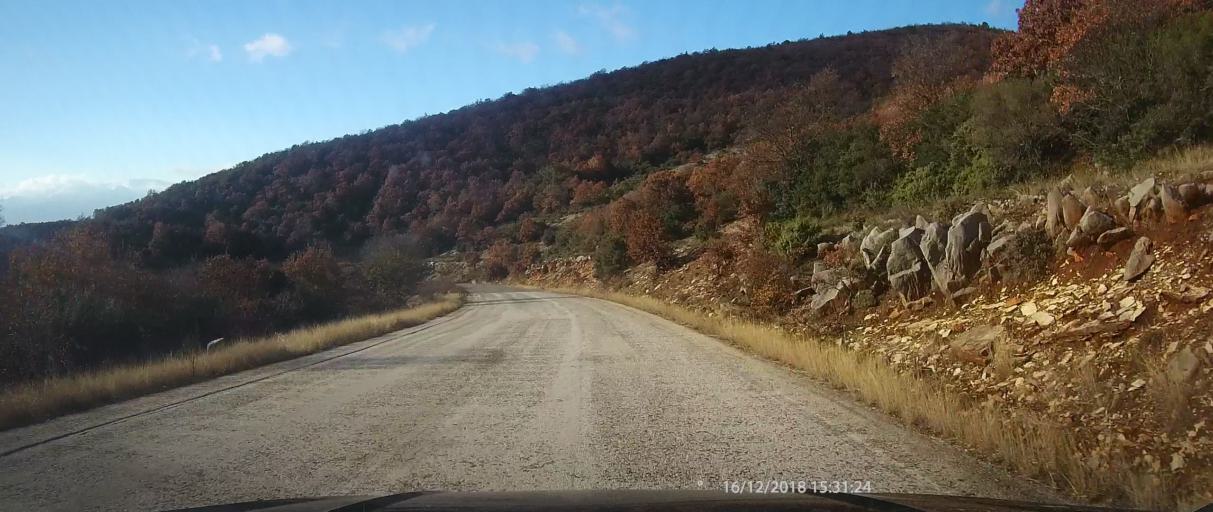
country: GR
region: Epirus
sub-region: Nomos Ioanninon
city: Konitsa
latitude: 40.0713
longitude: 20.7485
